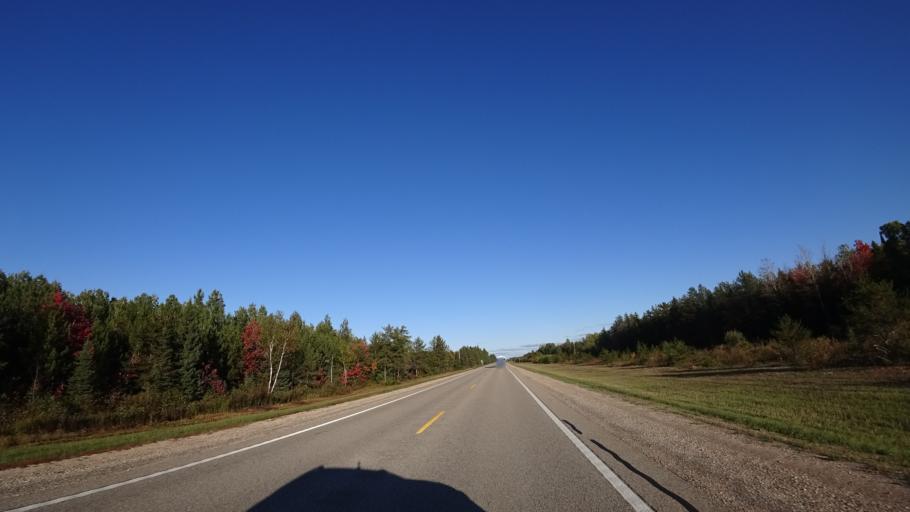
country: US
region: Michigan
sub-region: Schoolcraft County
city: Manistique
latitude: 46.3457
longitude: -86.1872
